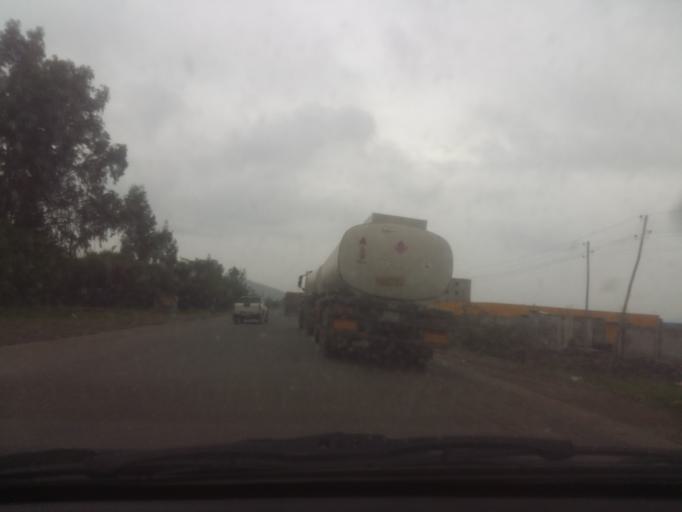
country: ET
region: Oromiya
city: Bishoftu
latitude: 8.8182
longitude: 38.8756
